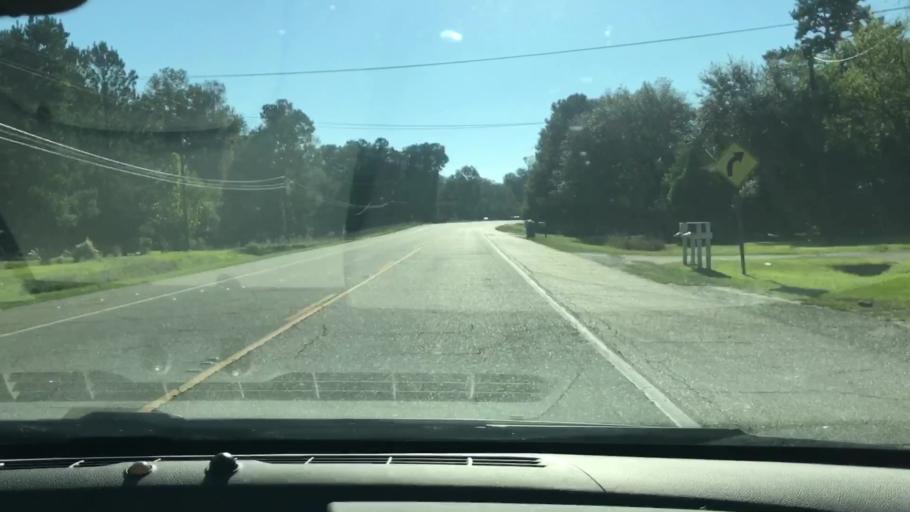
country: US
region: Louisiana
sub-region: Saint Tammany Parish
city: Pearl River
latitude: 30.4406
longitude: -89.7901
